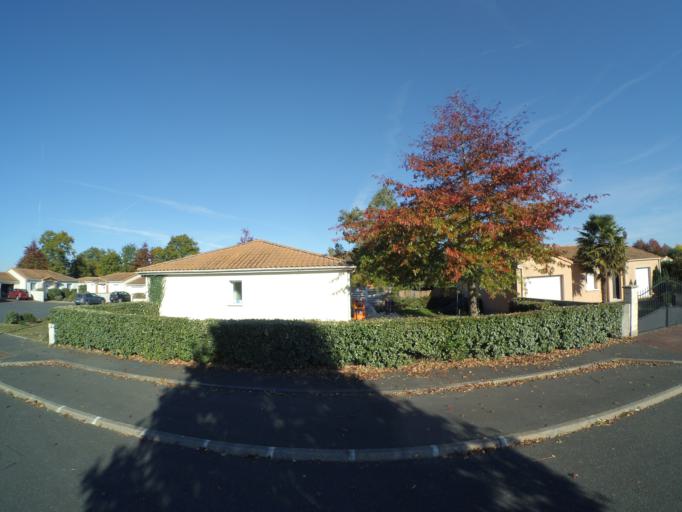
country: FR
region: Pays de la Loire
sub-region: Departement de la Loire-Atlantique
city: Saint-Lumine-de-Clisson
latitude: 47.0871
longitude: -1.3342
